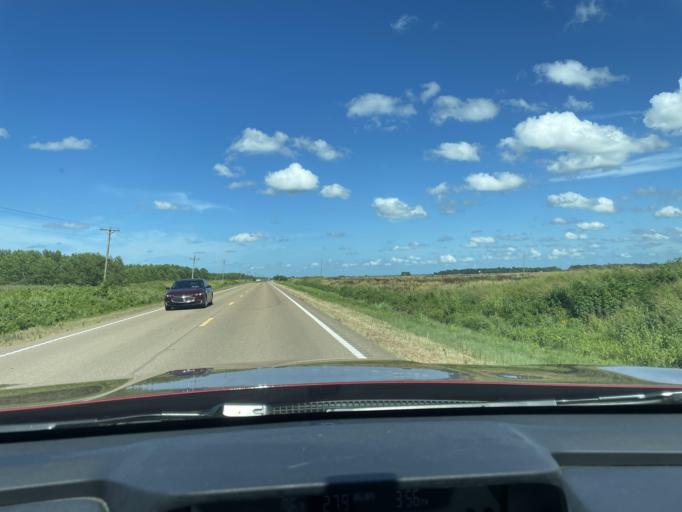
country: US
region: Mississippi
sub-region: Humphreys County
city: Belzoni
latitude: 33.1827
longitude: -90.6222
